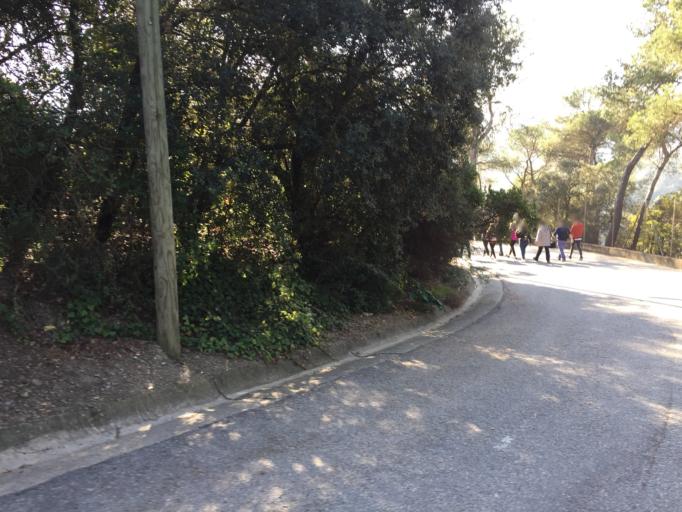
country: ES
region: Catalonia
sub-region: Provincia de Barcelona
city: Sant Just Desvern
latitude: 41.4224
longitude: 2.0969
